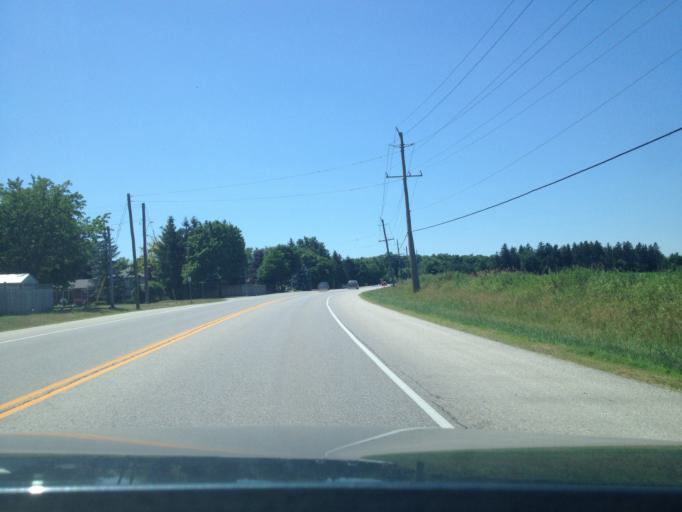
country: CA
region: Ontario
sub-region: Wellington County
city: Guelph
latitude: 43.6927
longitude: -80.3895
